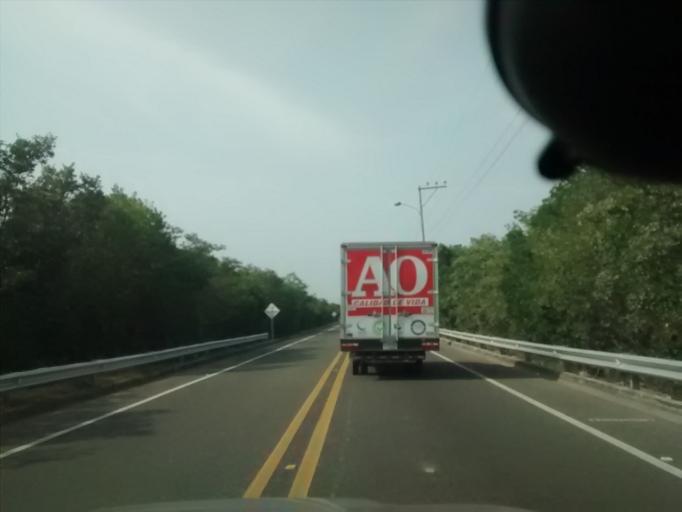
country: CO
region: Bolivar
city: Cartagena
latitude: 10.4859
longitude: -75.4854
